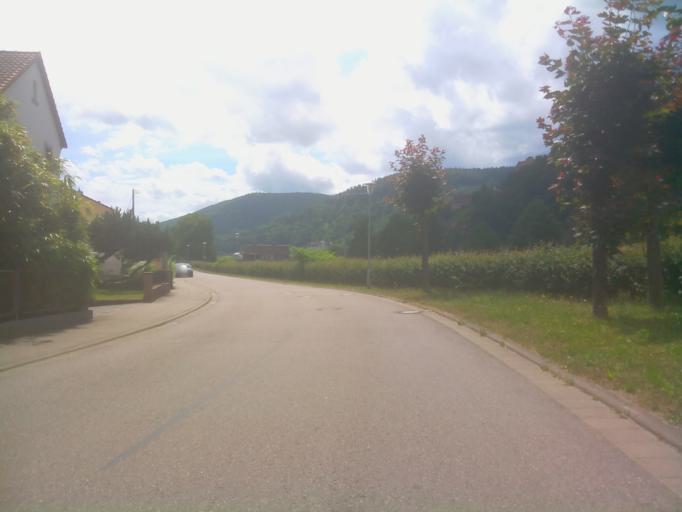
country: DE
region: Hesse
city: Hirschhorn
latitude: 49.4524
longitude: 8.9057
